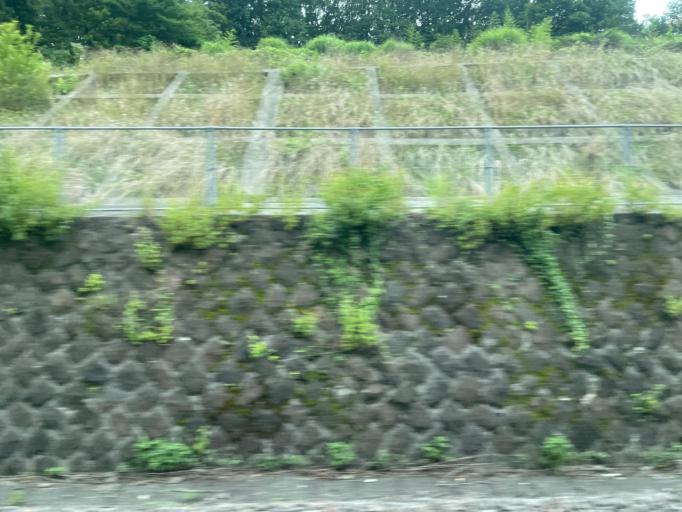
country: JP
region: Tochigi
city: Kuroiso
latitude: 37.0733
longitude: 140.1665
